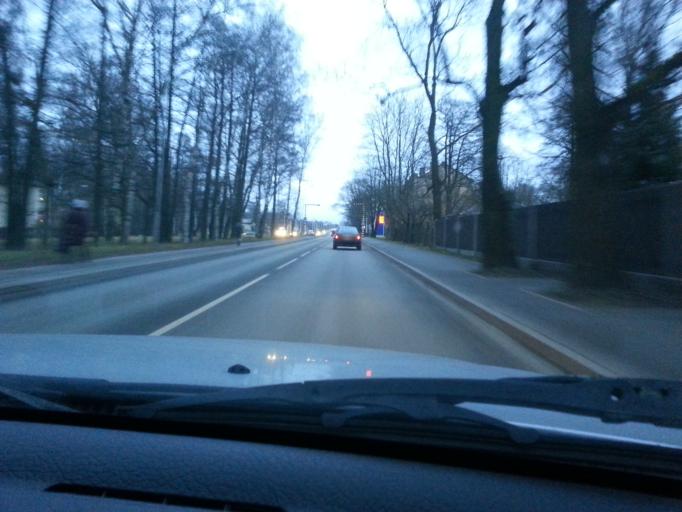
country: LV
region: Marupe
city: Marupe
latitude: 56.9521
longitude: 24.0321
